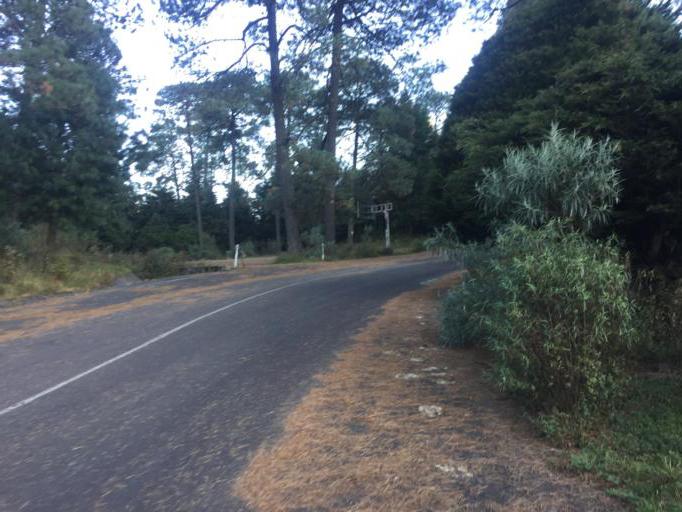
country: MX
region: Mexico City
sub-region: Tlalpan
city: Lomas de Tepemecatl
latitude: 19.2281
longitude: -99.2677
